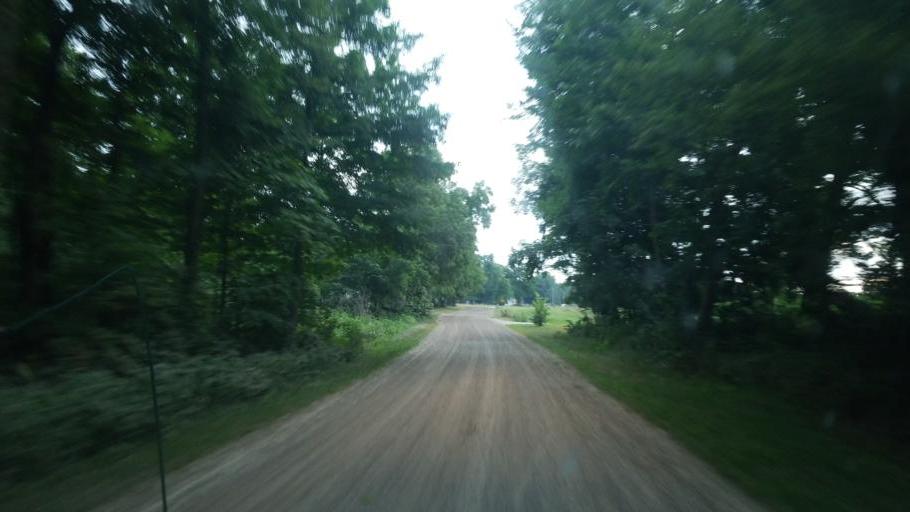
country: US
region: Ohio
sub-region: Defiance County
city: Hicksville
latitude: 41.3399
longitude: -84.8399
